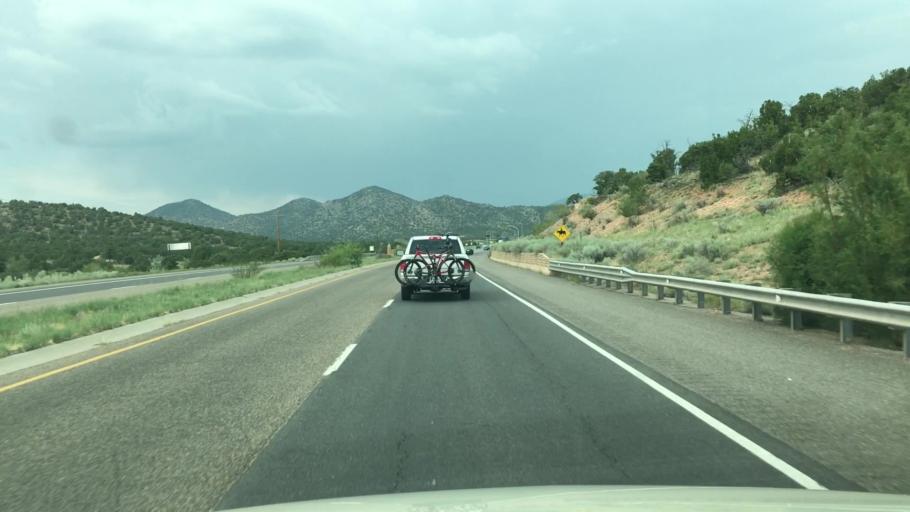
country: US
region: New Mexico
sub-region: Santa Fe County
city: Eldorado at Santa Fe
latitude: 35.5455
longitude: -105.8835
